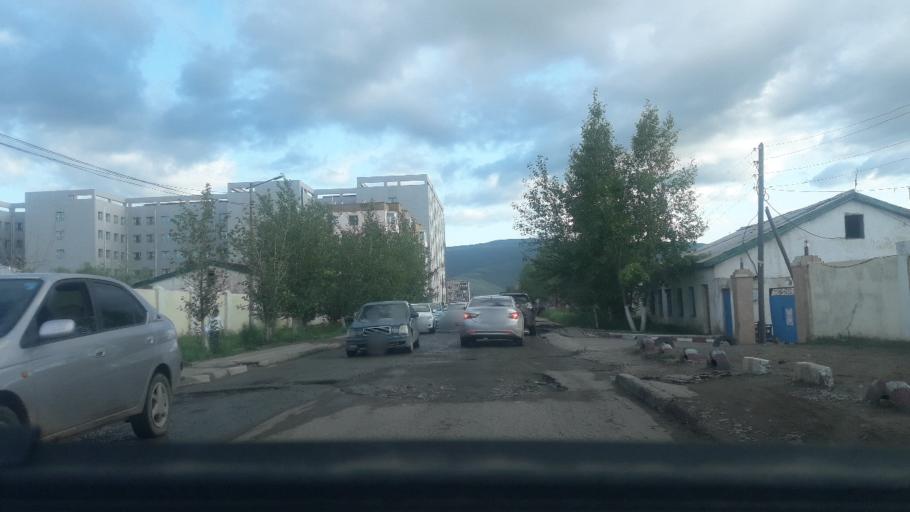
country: MN
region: Ulaanbaatar
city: Ulaanbaatar
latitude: 47.9166
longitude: 106.9945
